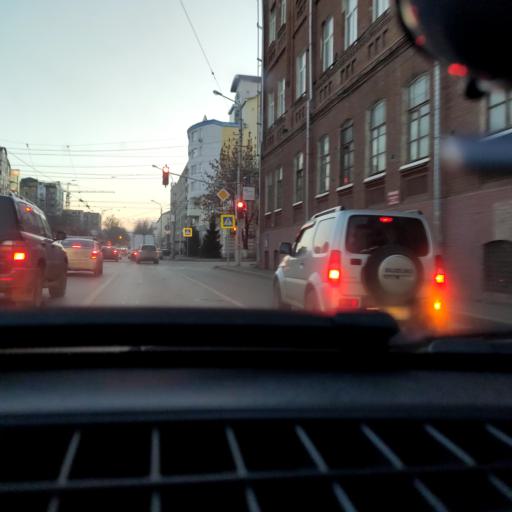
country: RU
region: Bashkortostan
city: Ufa
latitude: 54.7285
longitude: 55.9357
